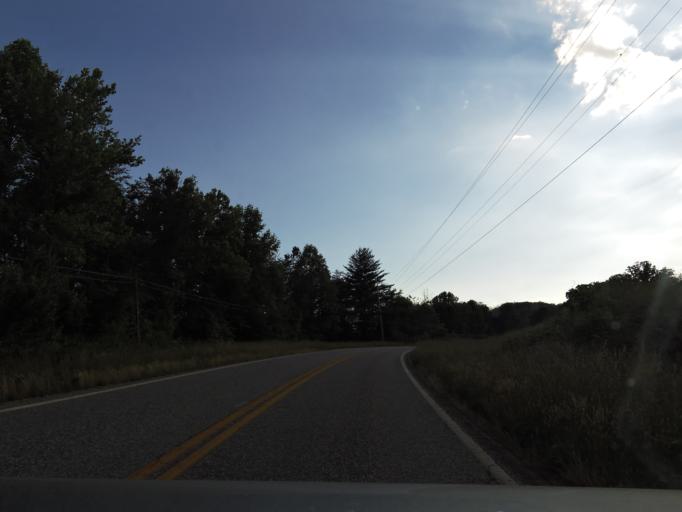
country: US
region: Georgia
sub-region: Union County
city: Blairsville
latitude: 34.7958
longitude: -83.8740
